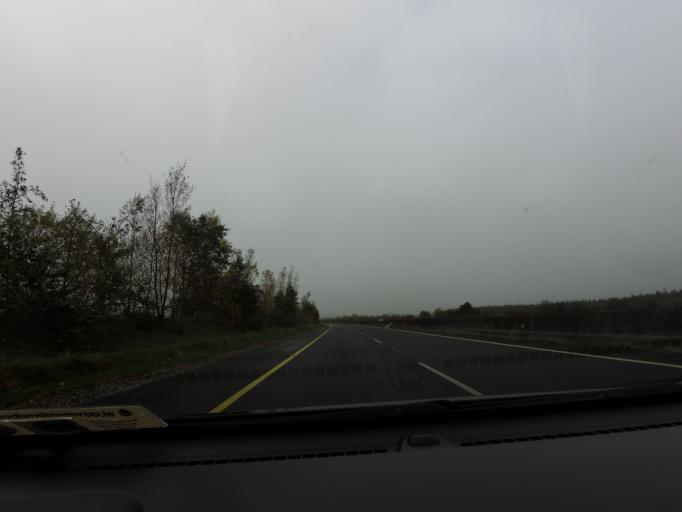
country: IE
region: Connaught
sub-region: County Galway
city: Ballinasloe
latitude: 53.3078
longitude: -8.3018
